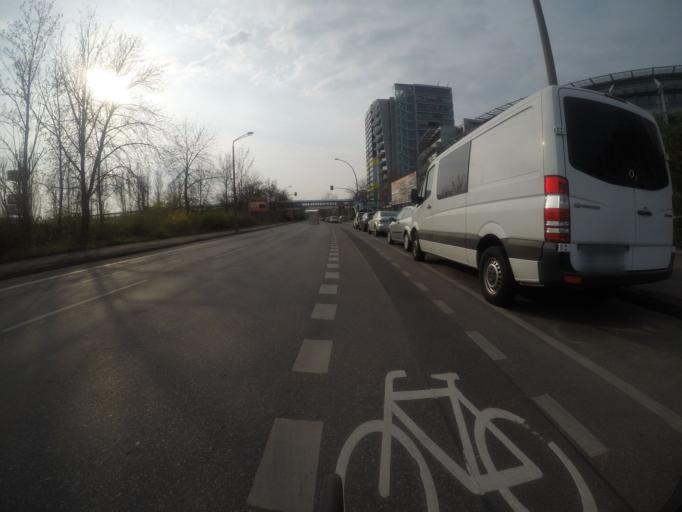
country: DE
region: Berlin
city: Fennpfuhl
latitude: 52.5241
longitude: 13.4667
